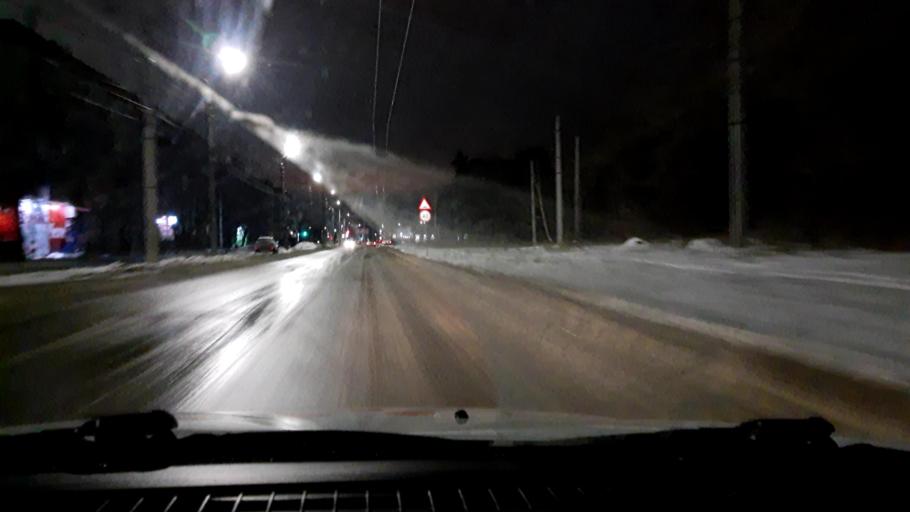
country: RU
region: Nizjnij Novgorod
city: Dzerzhinsk
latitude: 56.2291
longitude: 43.4471
